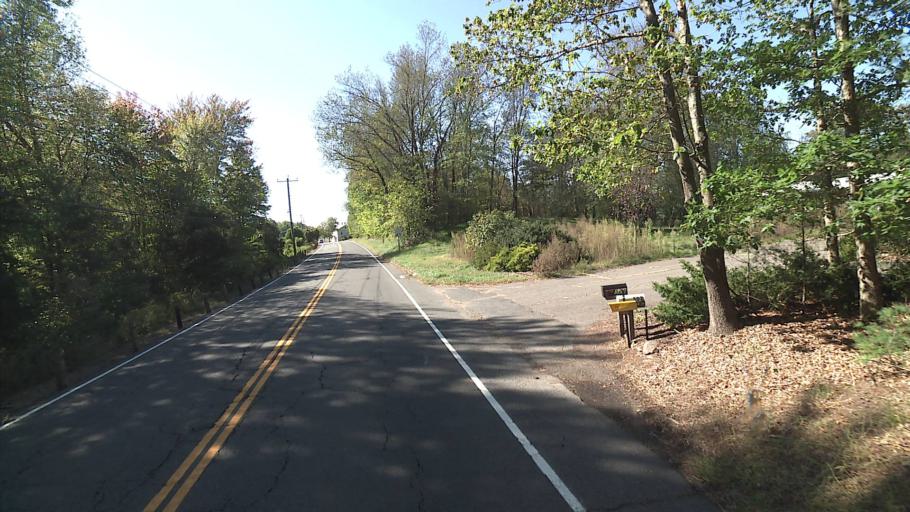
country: US
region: Connecticut
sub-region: Tolland County
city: Somers
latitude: 41.9525
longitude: -72.4478
